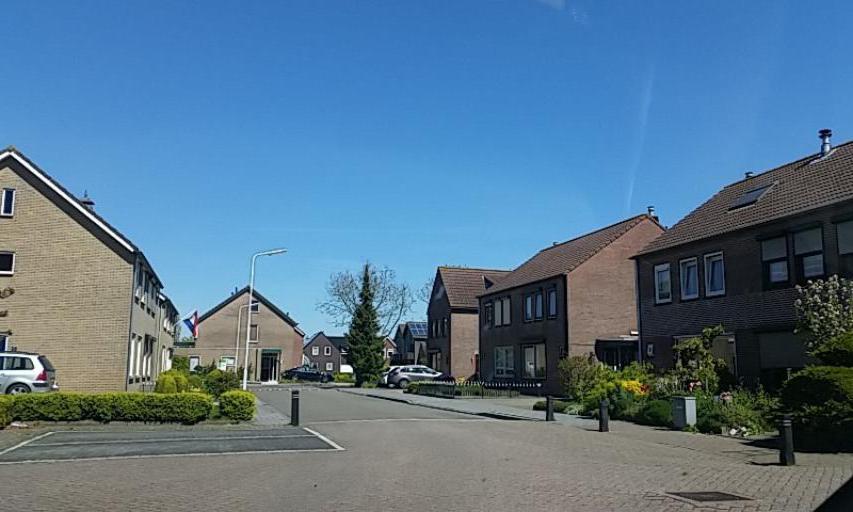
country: NL
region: Zeeland
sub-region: Gemeente Terneuzen
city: Terneuzen
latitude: 51.3071
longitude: 3.7757
